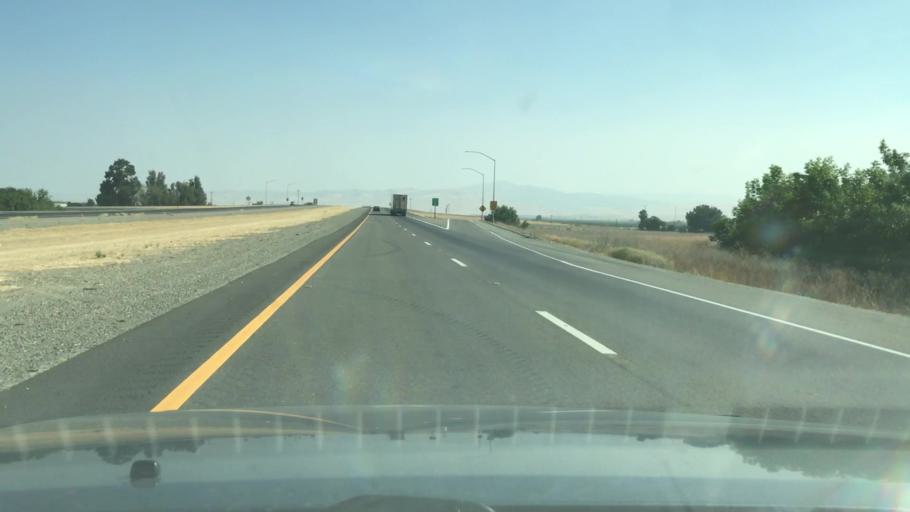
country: US
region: California
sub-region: San Joaquin County
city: Tracy
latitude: 37.6873
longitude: -121.3435
